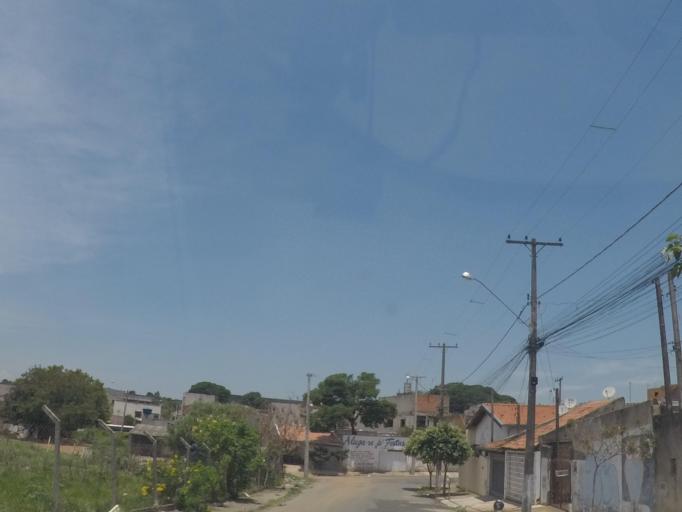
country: BR
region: Sao Paulo
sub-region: Hortolandia
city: Hortolandia
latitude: -22.8513
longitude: -47.1854
